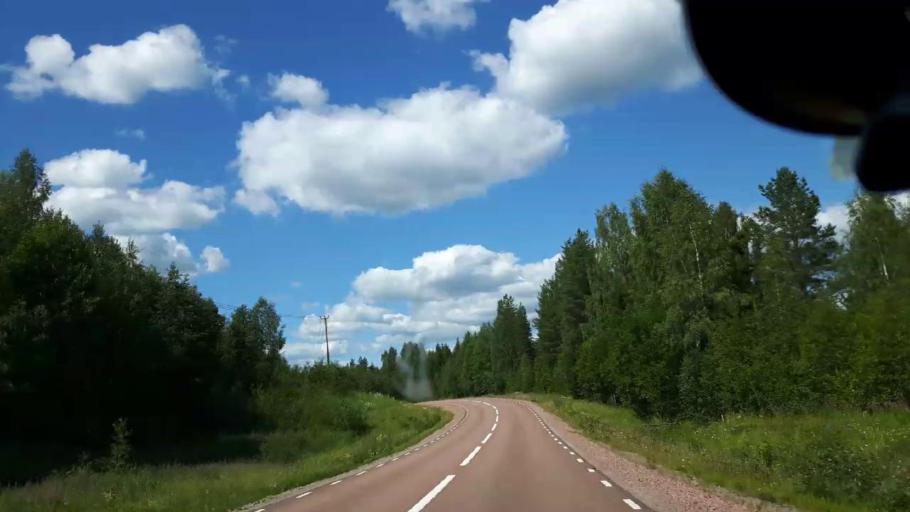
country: SE
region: Jaemtland
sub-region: Ragunda Kommun
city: Hammarstrand
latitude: 63.0151
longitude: 16.6205
